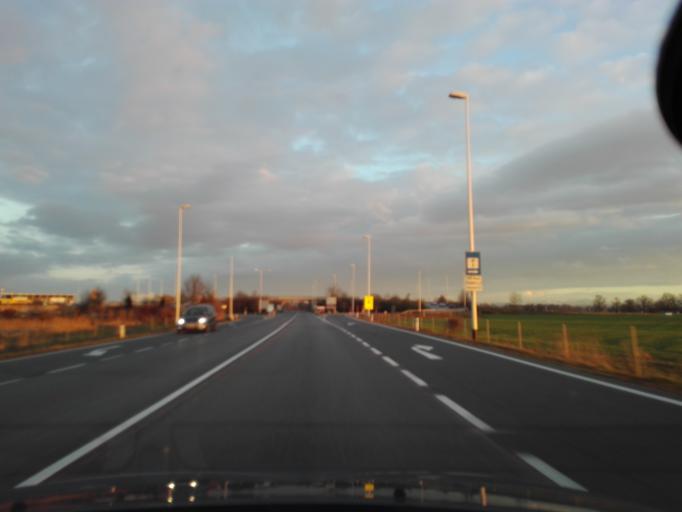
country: AT
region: Upper Austria
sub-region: Politischer Bezirk Perg
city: Perg
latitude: 48.2377
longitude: 14.6206
